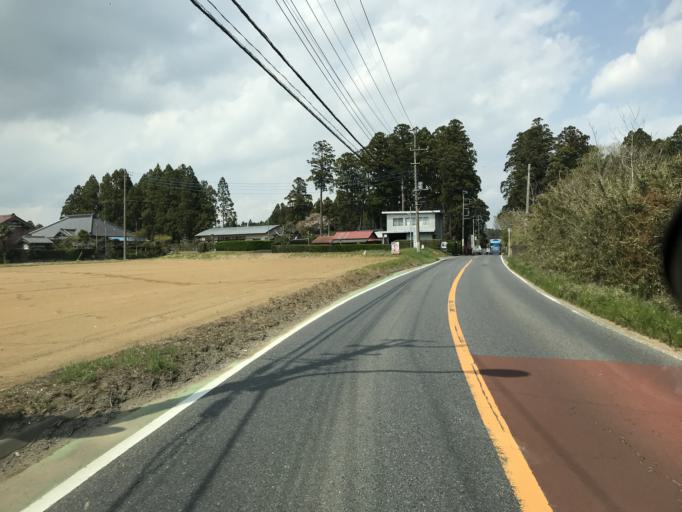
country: JP
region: Chiba
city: Sawara
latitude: 35.8661
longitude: 140.5426
